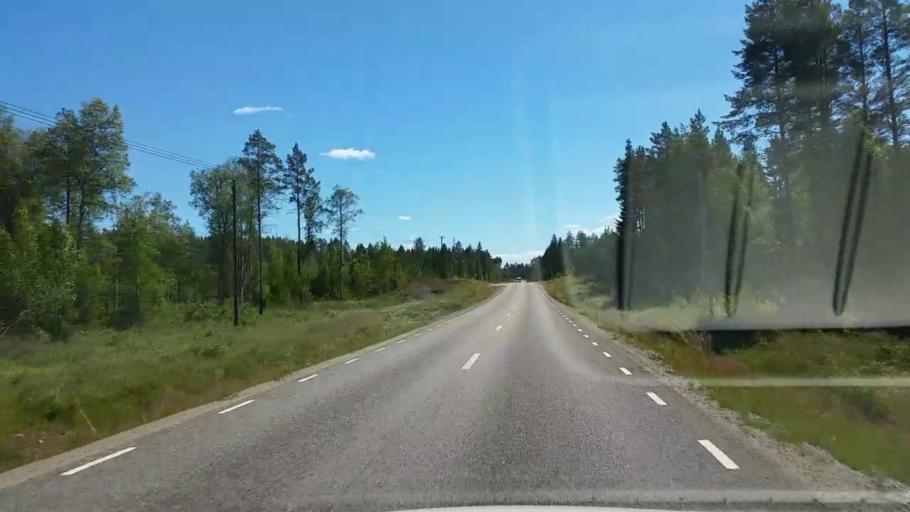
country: SE
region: Gaevleborg
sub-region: Ovanakers Kommun
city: Edsbyn
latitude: 61.4654
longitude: 15.6977
